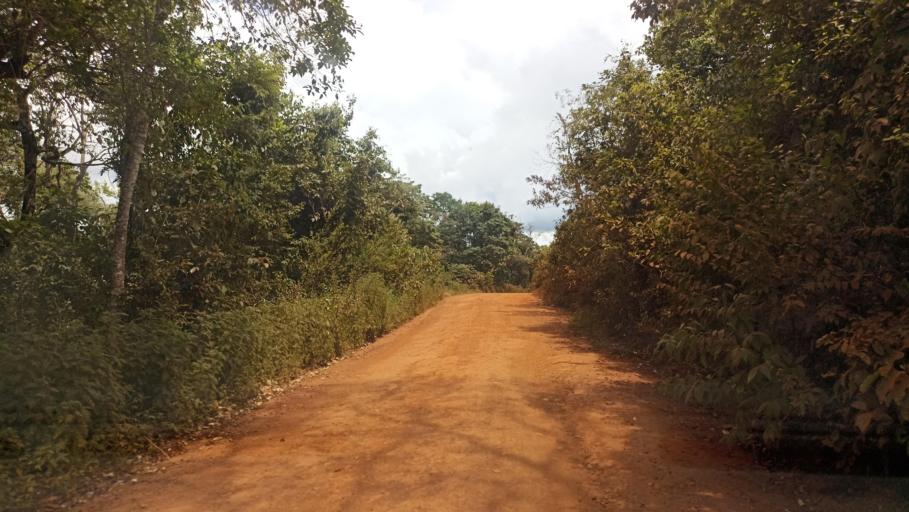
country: BR
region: Minas Gerais
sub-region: Itabirito
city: Itabirito
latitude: -20.3451
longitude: -43.7485
